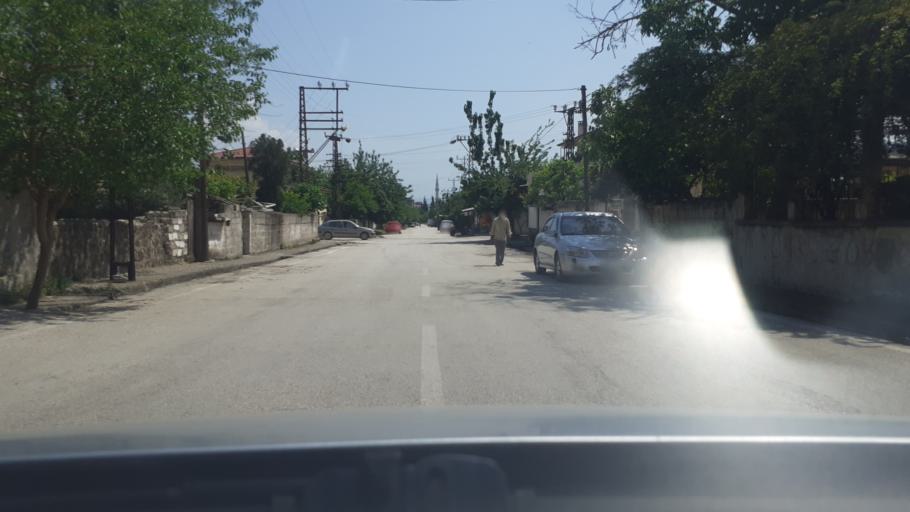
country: TR
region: Hatay
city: Kirikhan
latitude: 36.4912
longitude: 36.3540
